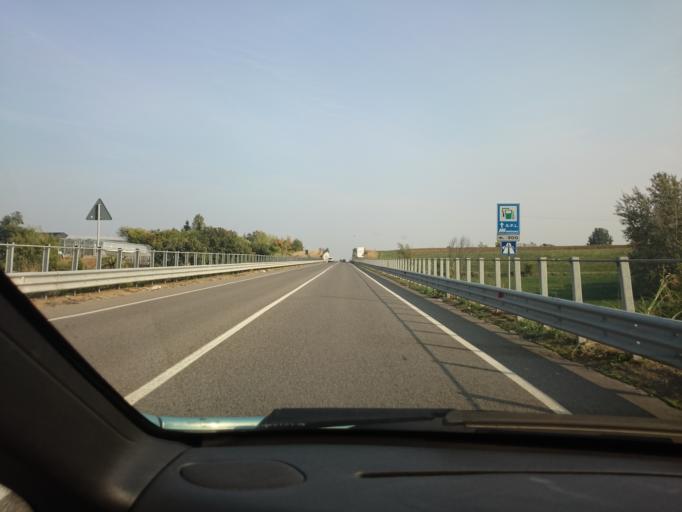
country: IT
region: Emilia-Romagna
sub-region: Provincia di Reggio Emilia
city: Scandiano
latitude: 44.5929
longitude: 10.7100
